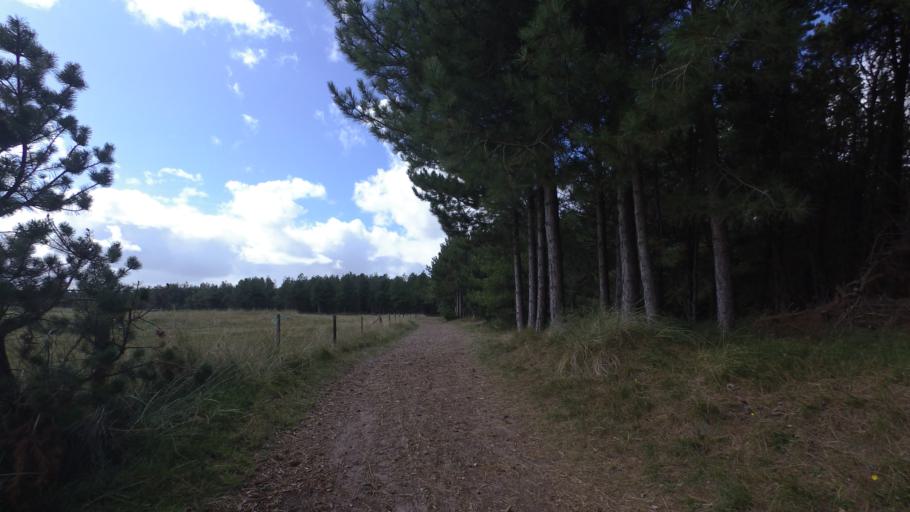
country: NL
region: Friesland
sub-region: Gemeente Ameland
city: Nes
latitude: 53.4539
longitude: 5.7880
